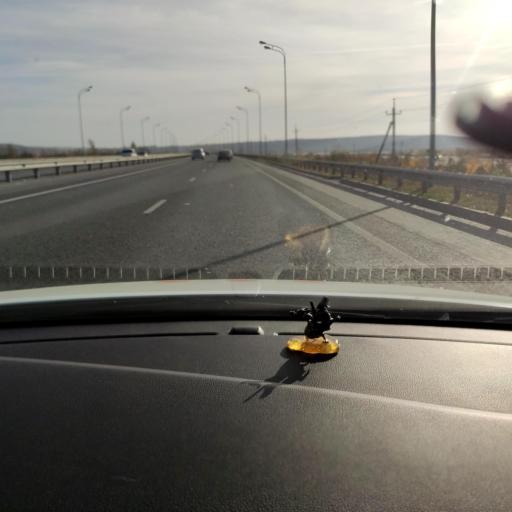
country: RU
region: Tatarstan
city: Osinovo
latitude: 55.8156
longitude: 48.8423
